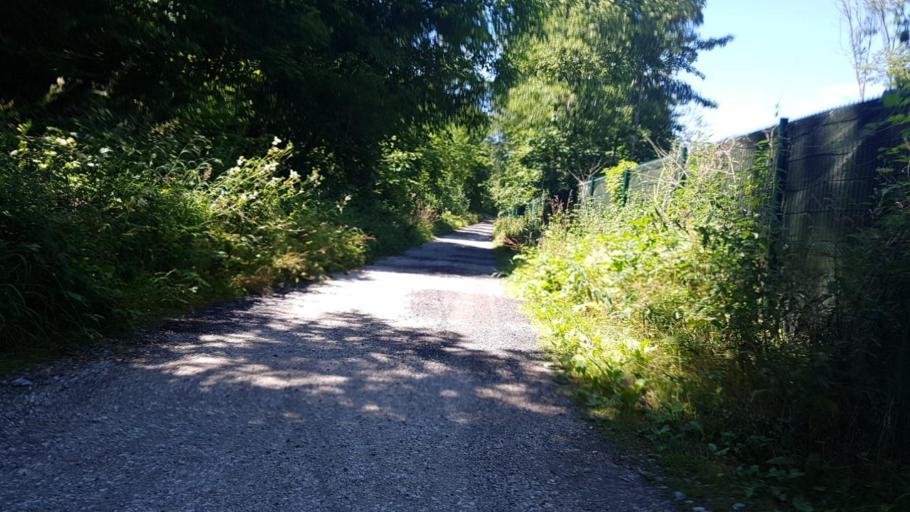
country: FR
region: Ile-de-France
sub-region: Departement de Seine-et-Marne
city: Nanteuil-les-Meaux
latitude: 48.9370
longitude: 2.8909
